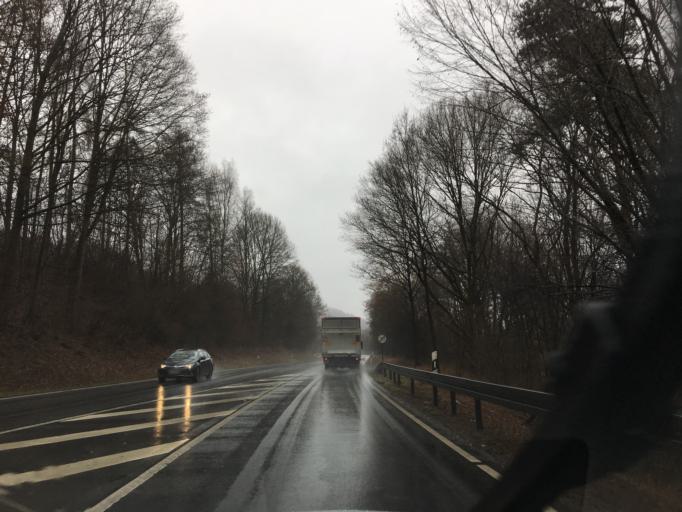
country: DE
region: Hesse
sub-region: Regierungsbezirk Darmstadt
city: Bad Konig
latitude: 49.7145
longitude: 8.9907
